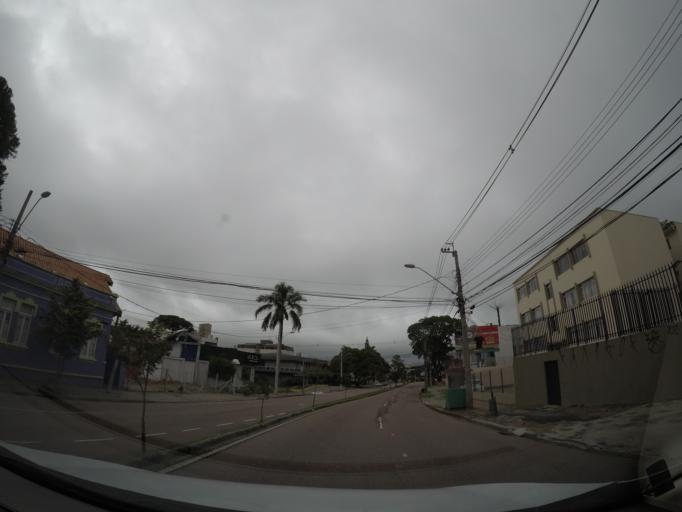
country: BR
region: Parana
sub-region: Curitiba
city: Curitiba
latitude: -25.4486
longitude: -49.2983
